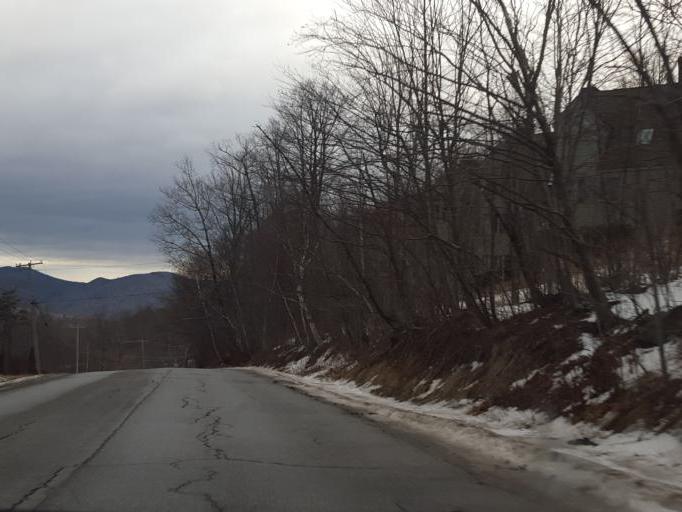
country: US
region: Vermont
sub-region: Rutland County
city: Rutland
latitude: 43.6257
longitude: -72.7858
